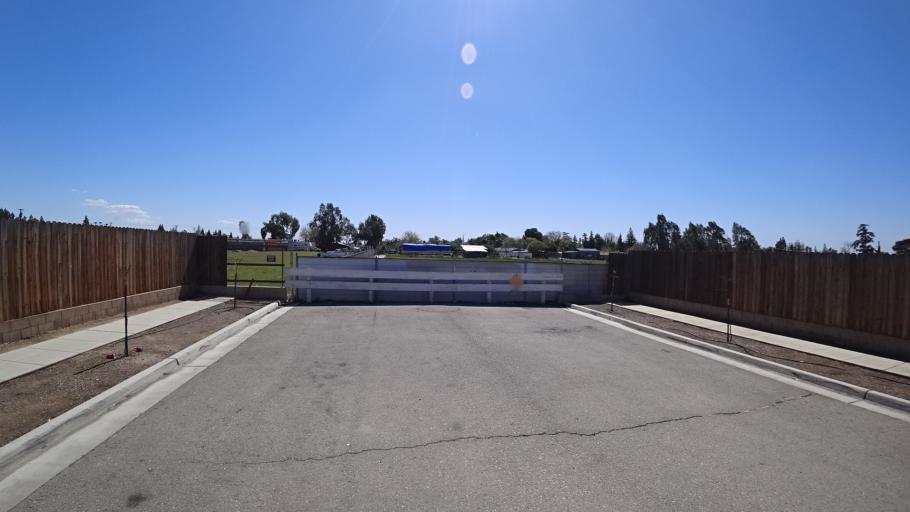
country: US
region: California
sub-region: Fresno County
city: West Park
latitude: 36.7883
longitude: -119.8686
